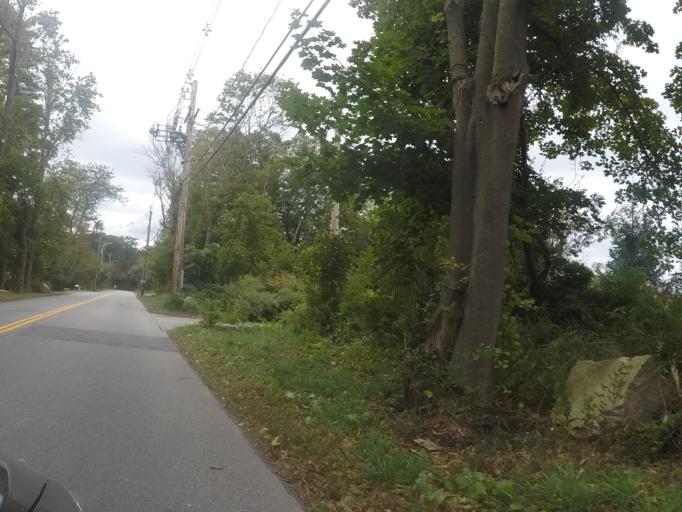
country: US
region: Massachusetts
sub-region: Bristol County
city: Smith Mills
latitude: 41.6807
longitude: -71.0307
